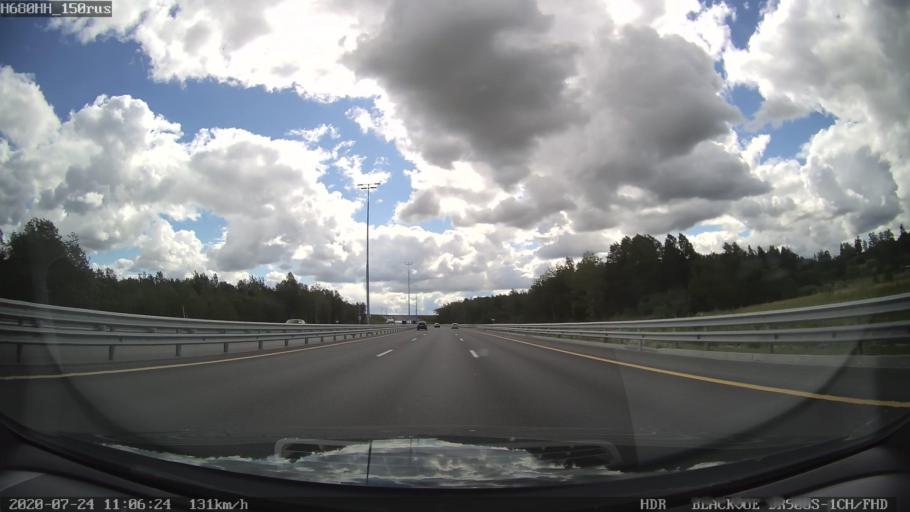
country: RU
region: St.-Petersburg
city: Shushary
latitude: 59.7636
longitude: 30.3742
